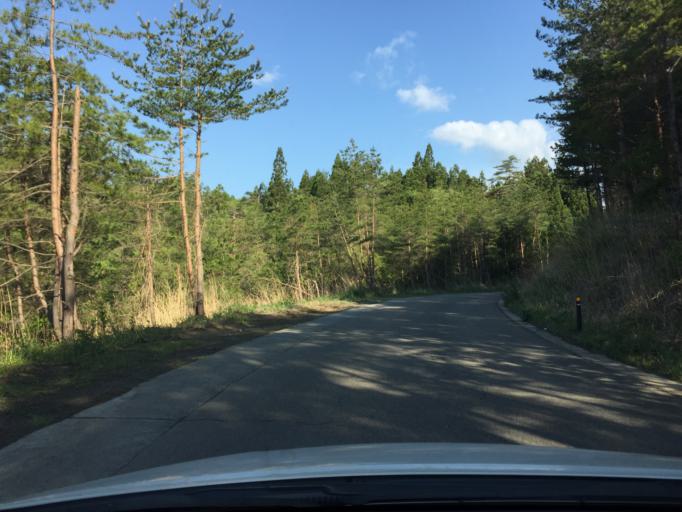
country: JP
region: Fukushima
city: Kitakata
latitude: 37.6691
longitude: 139.8365
